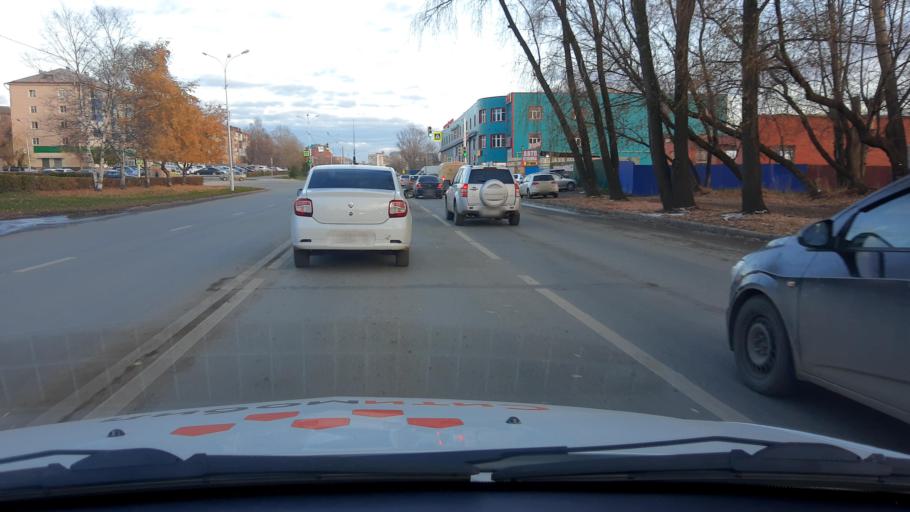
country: RU
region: Bashkortostan
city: Ufa
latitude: 54.8080
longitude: 56.0965
